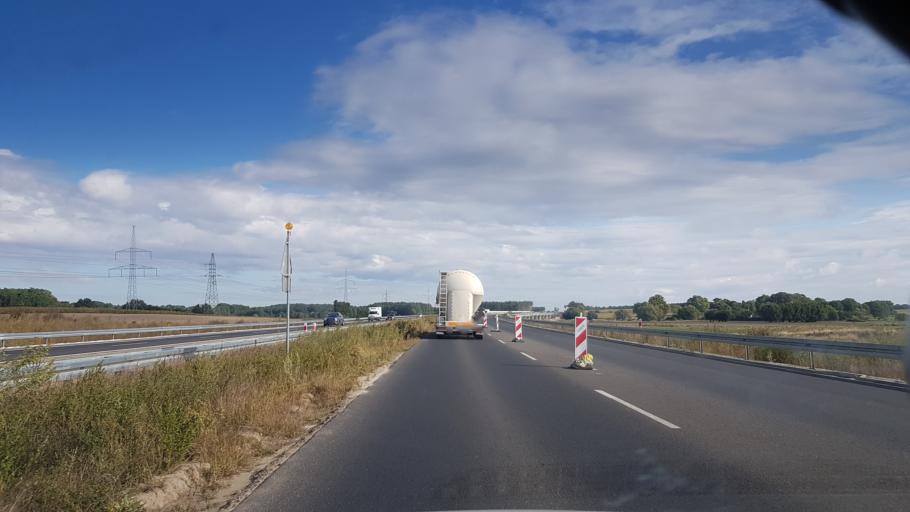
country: PL
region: Greater Poland Voivodeship
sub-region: Powiat poznanski
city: Steszew
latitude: 52.2875
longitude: 16.6759
